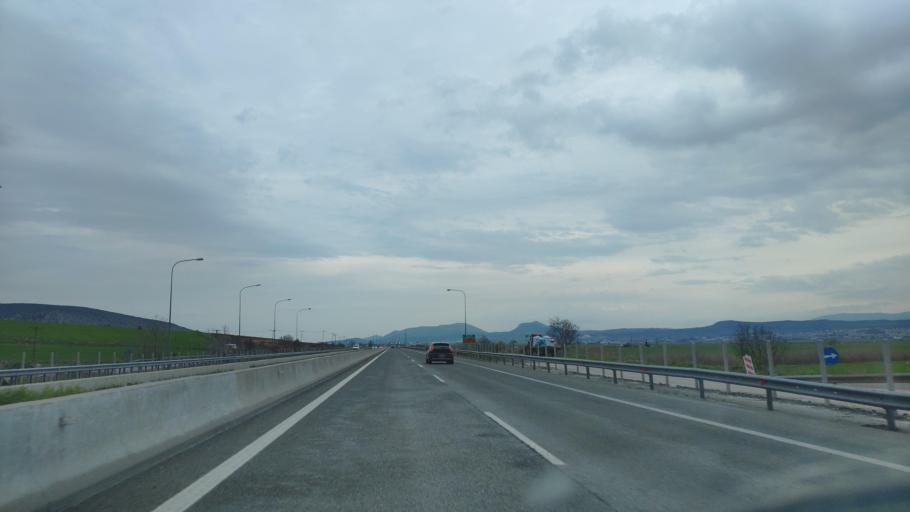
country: GR
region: Central Greece
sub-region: Nomos Voiotias
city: Thivai
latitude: 38.3751
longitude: 23.2702
